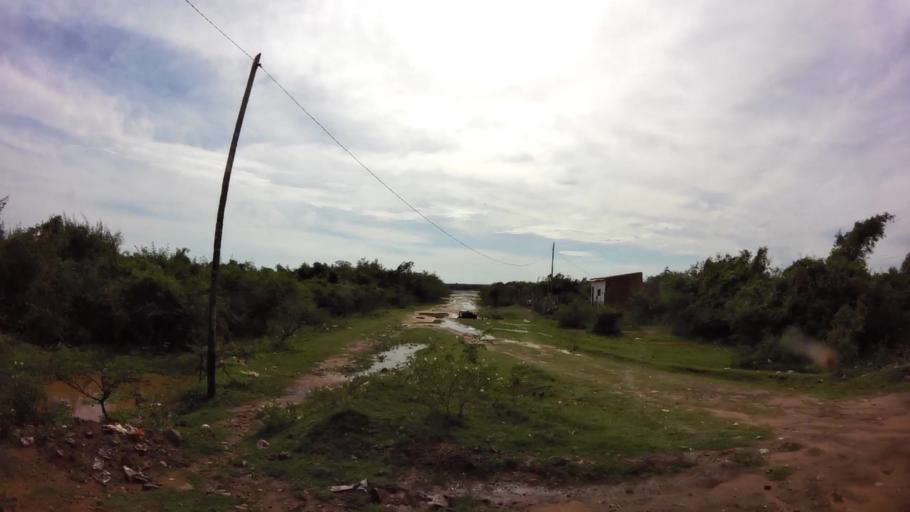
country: PY
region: Central
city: Limpio
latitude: -25.1204
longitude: -57.4820
